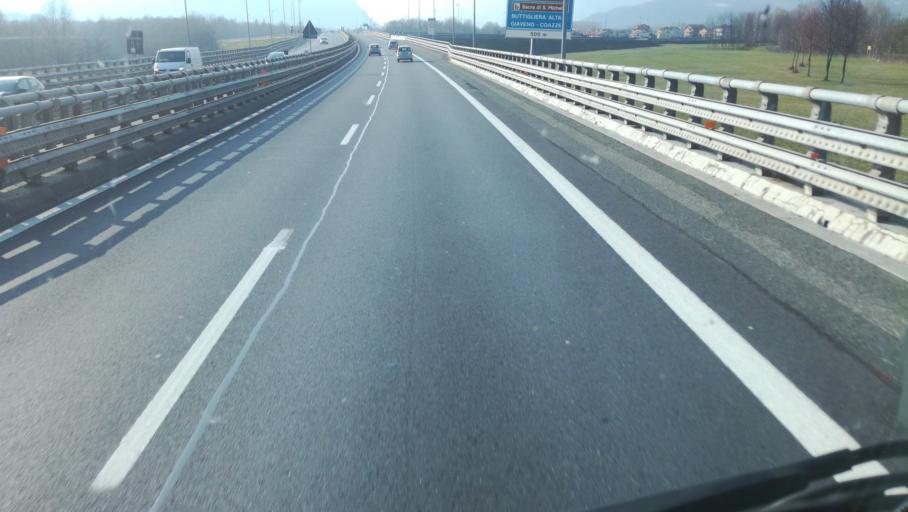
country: IT
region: Piedmont
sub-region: Provincia di Torino
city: Drubiaglio-Grangia
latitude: 45.0908
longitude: 7.4241
